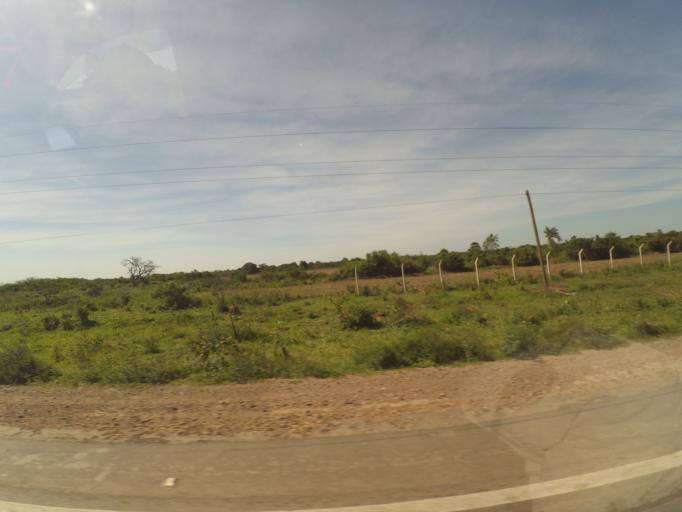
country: BO
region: Santa Cruz
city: San Julian
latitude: -17.7321
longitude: -62.9285
